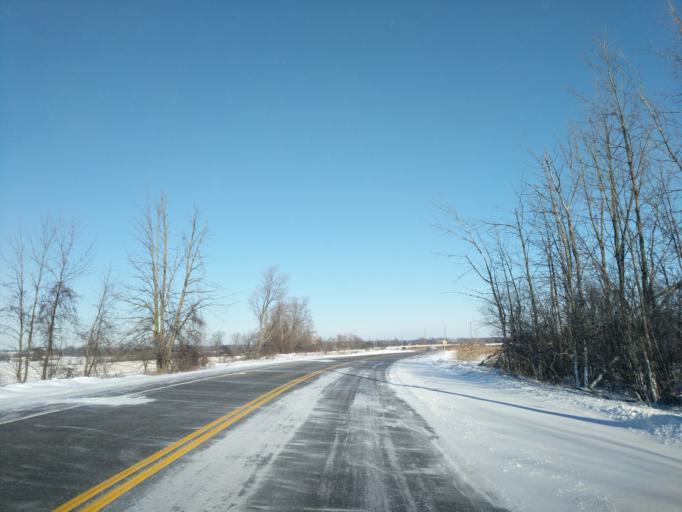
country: CA
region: Ontario
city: Pickering
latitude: 43.8535
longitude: -79.1308
